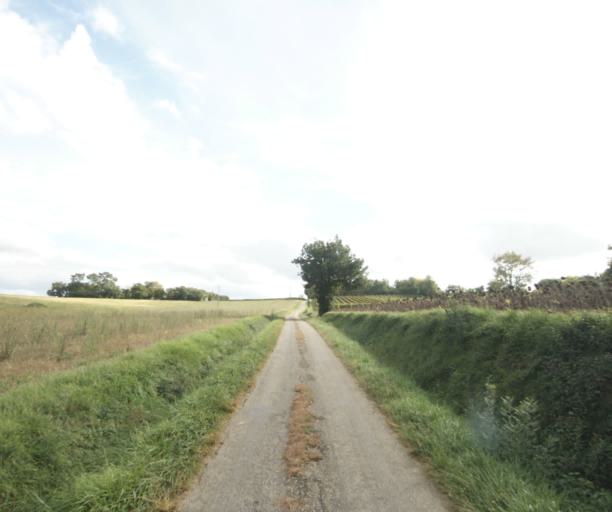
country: FR
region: Midi-Pyrenees
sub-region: Departement du Gers
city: Gondrin
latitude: 43.8579
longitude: 0.2718
